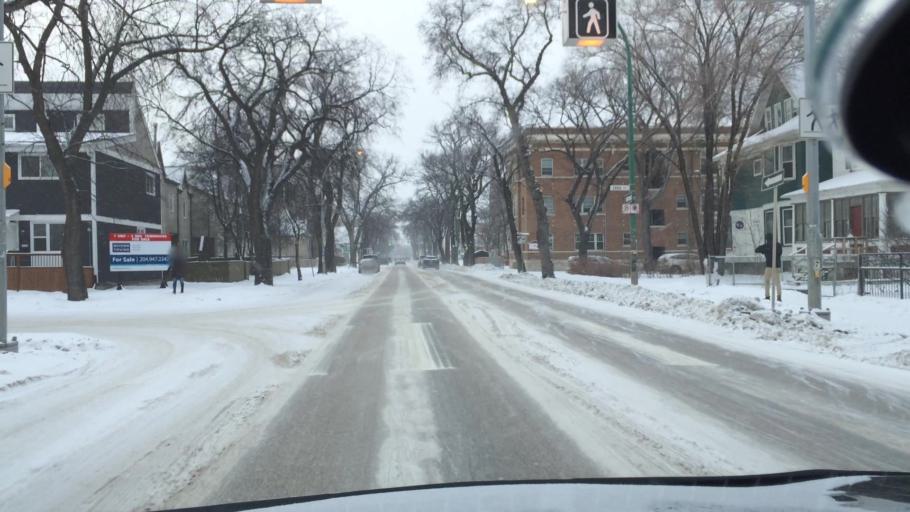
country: CA
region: Manitoba
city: Winnipeg
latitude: 49.8841
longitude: -97.1608
